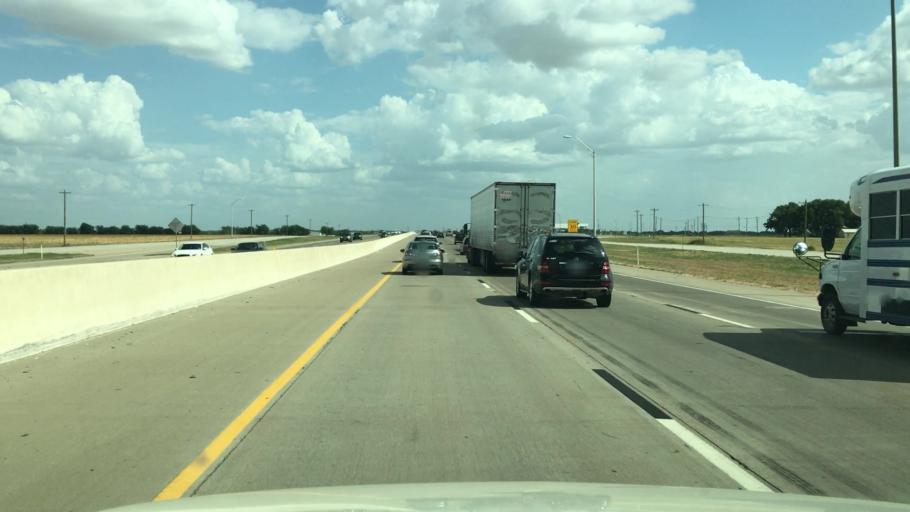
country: US
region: Texas
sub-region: Hill County
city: Hillsboro
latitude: 31.9328
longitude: -97.1049
